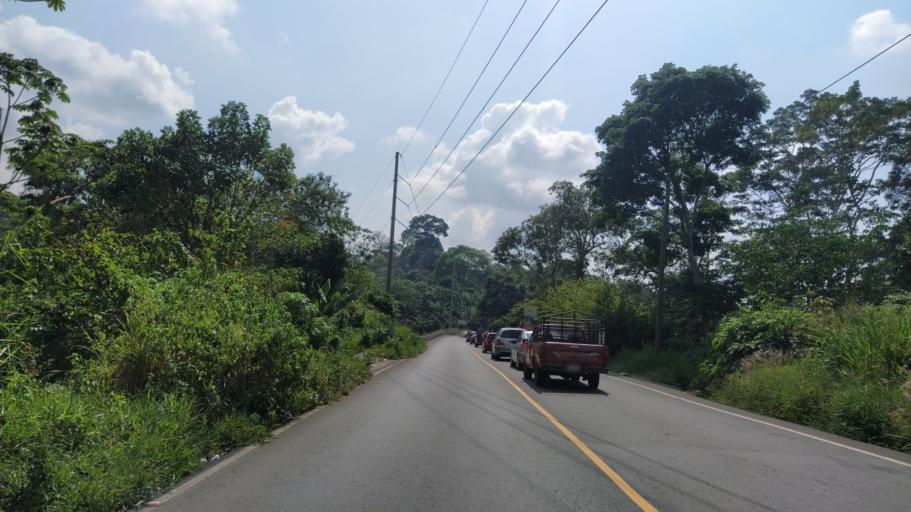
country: GT
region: Quetzaltenango
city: El Palmar
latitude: 14.6409
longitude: -91.5757
